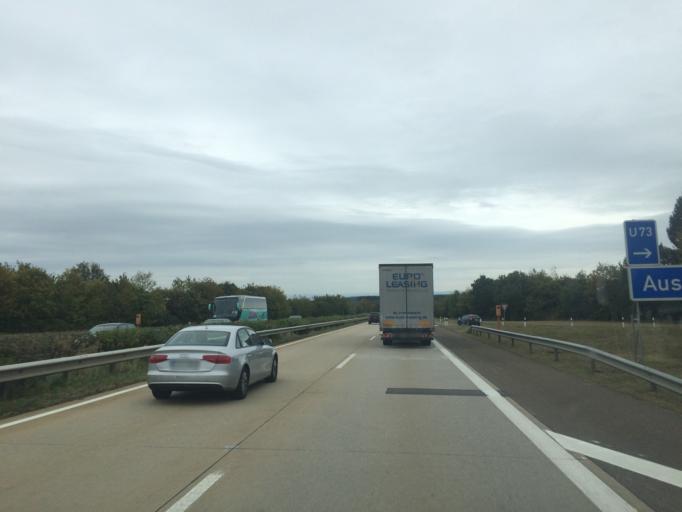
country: DE
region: Rheinland-Pfalz
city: Laufeld
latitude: 50.1010
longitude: 6.8638
